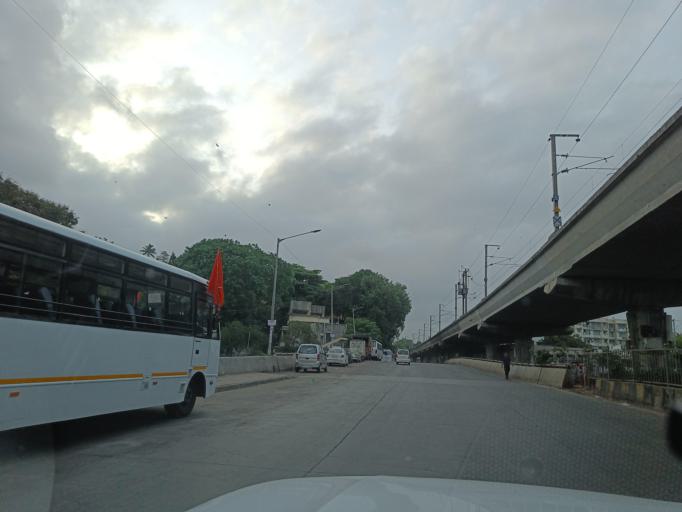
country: IN
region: Maharashtra
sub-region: Mumbai Suburban
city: Powai
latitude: 19.0922
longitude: 72.9027
